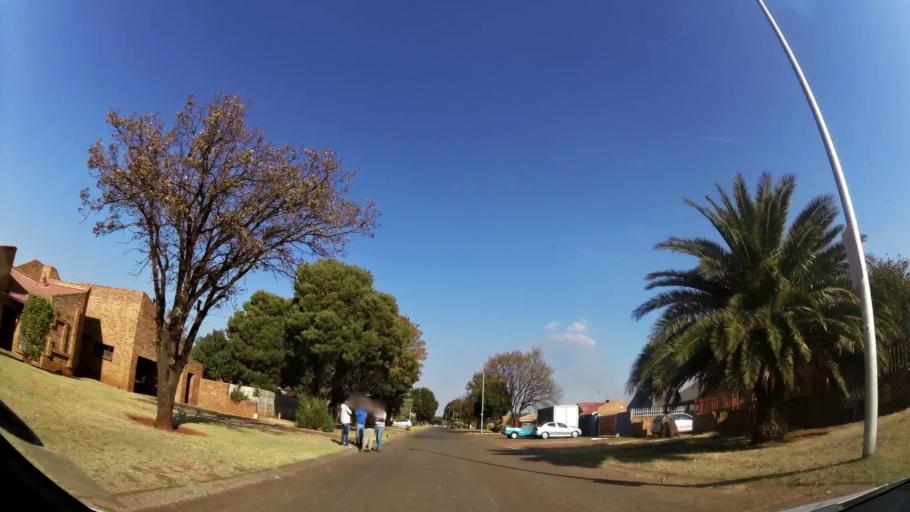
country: ZA
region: Gauteng
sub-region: Ekurhuleni Metropolitan Municipality
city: Brakpan
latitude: -26.2306
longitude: 28.3327
